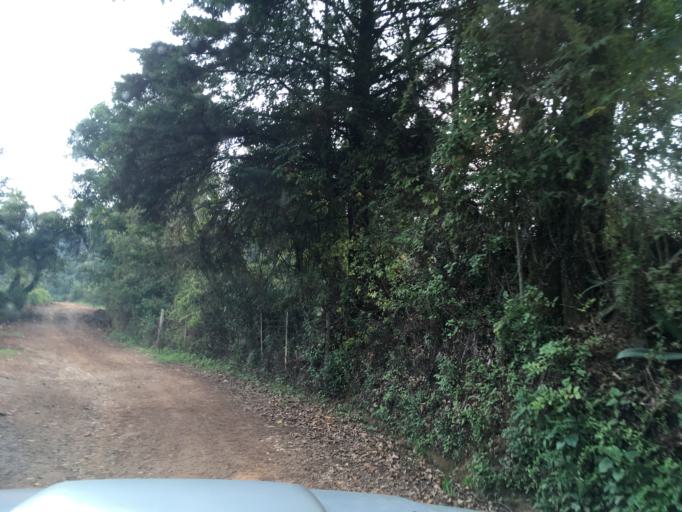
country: MX
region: Michoacan
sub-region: Zitacuaro
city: La Fundicion (Quinta Manzana)
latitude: 19.4906
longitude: -100.3146
